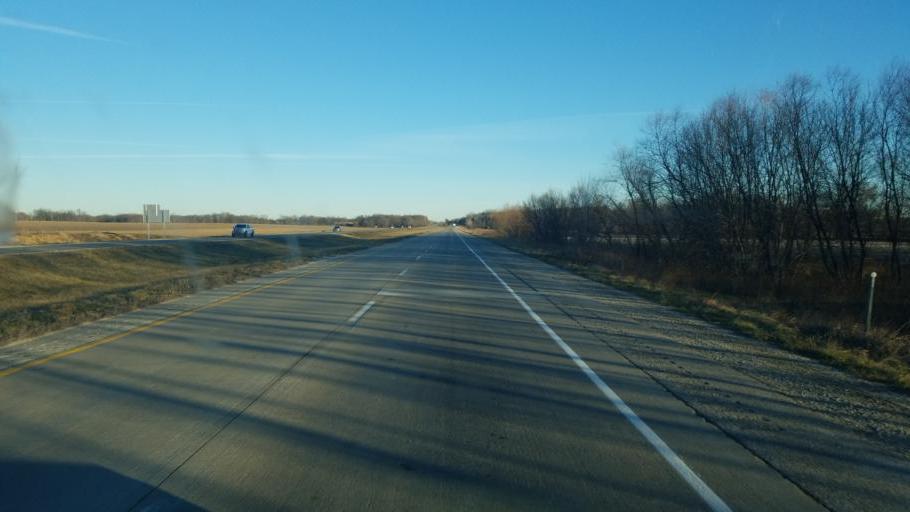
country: US
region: Iowa
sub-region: Wapello County
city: Eddyville
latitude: 41.1908
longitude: -92.6399
